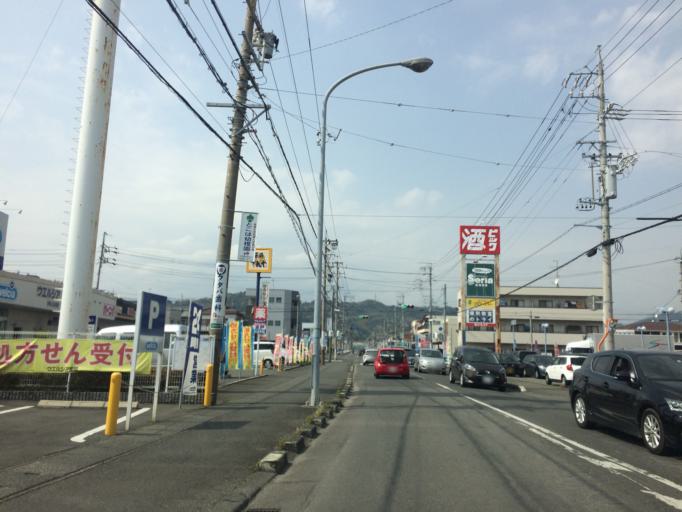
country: JP
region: Shizuoka
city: Shizuoka-shi
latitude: 34.9977
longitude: 138.3950
